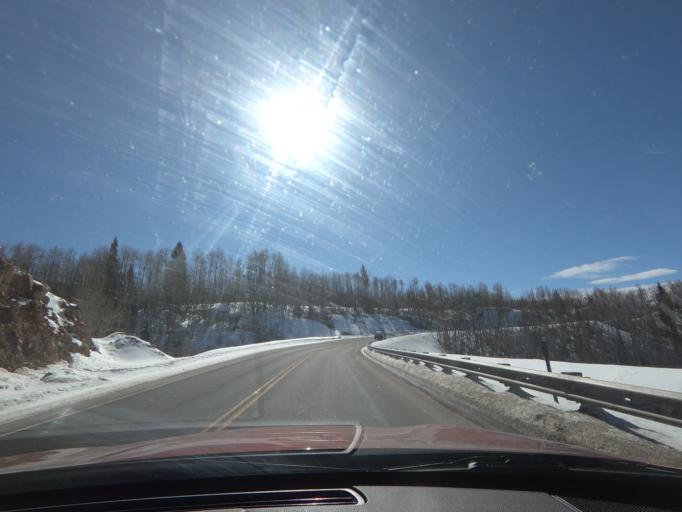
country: US
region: Colorado
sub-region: Teller County
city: Cripple Creek
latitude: 38.8008
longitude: -105.1186
